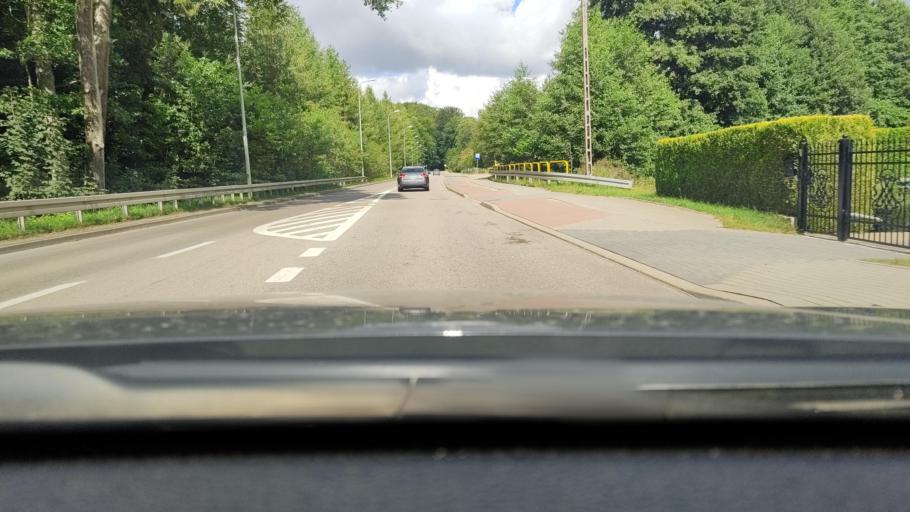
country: PL
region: Pomeranian Voivodeship
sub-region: Powiat wejherowski
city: Wejherowo
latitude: 54.5907
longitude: 18.2417
